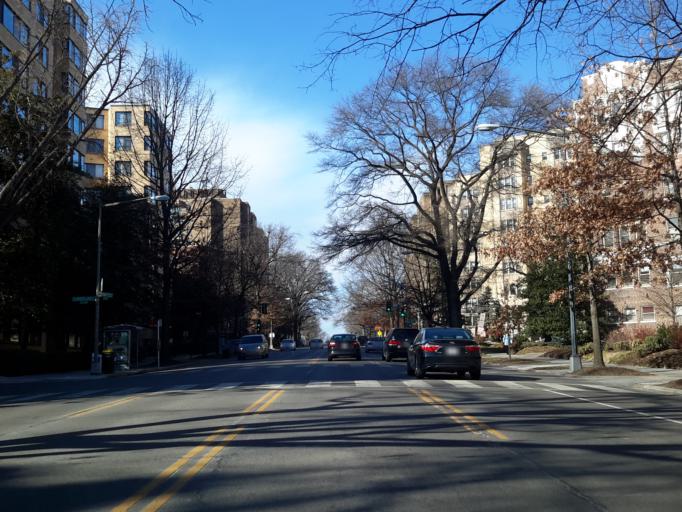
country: US
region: Maryland
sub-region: Montgomery County
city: Chevy Chase Village
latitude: 38.9511
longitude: -77.0675
